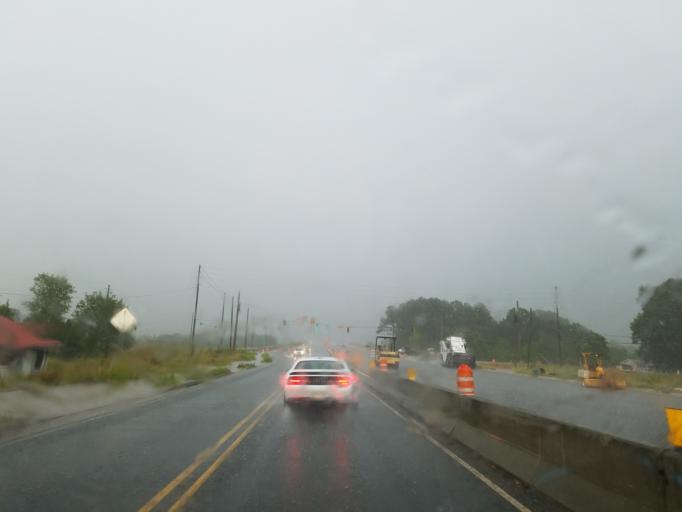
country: US
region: Georgia
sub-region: Bartow County
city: Adairsville
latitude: 34.3768
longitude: -84.9422
